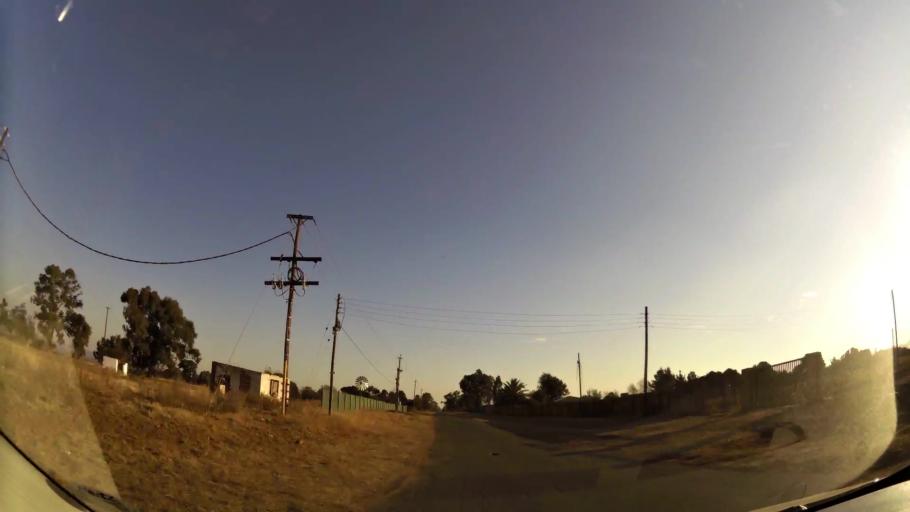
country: ZA
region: Gauteng
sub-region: West Rand District Municipality
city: Randfontein
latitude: -26.2134
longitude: 27.6573
